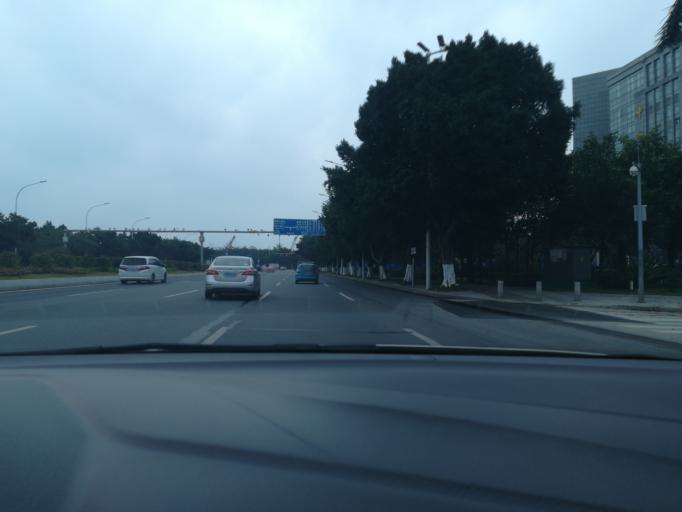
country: CN
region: Guangdong
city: Nansha
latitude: 22.8007
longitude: 113.5800
